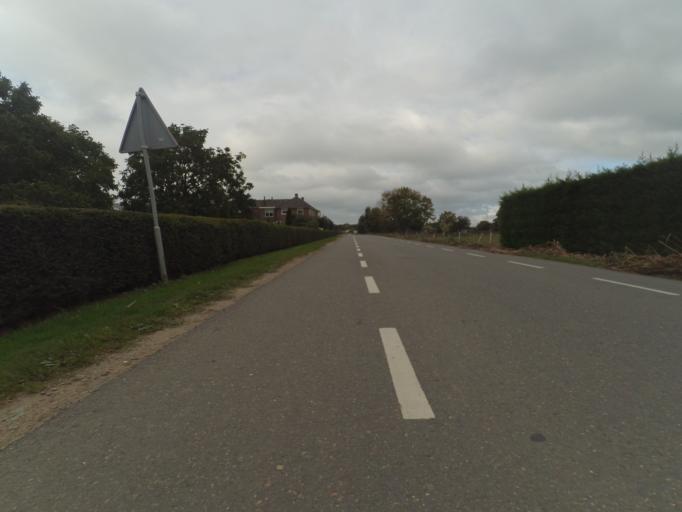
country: NL
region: Utrecht
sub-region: Gemeente Utrechtse Heuvelrug
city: Amerongen
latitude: 51.9618
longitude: 5.4730
